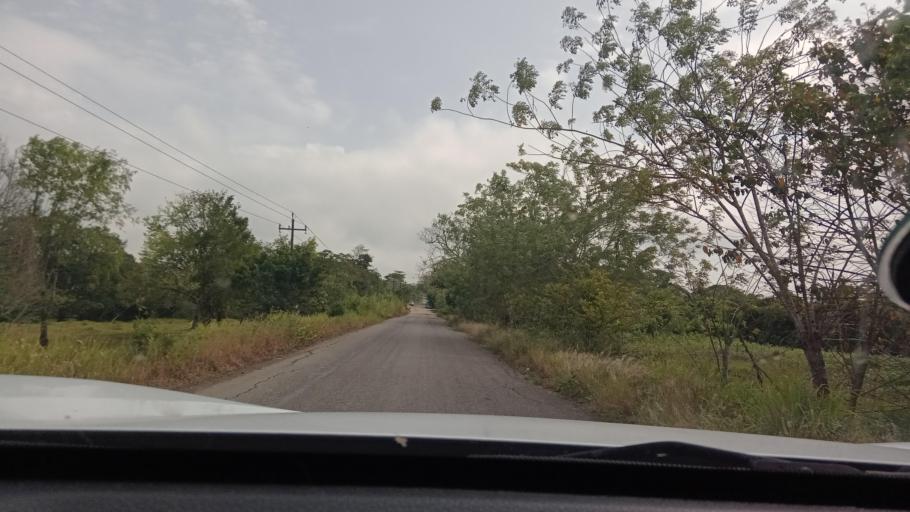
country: MX
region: Tabasco
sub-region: Huimanguillo
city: Francisco Rueda
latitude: 17.5625
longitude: -94.1161
